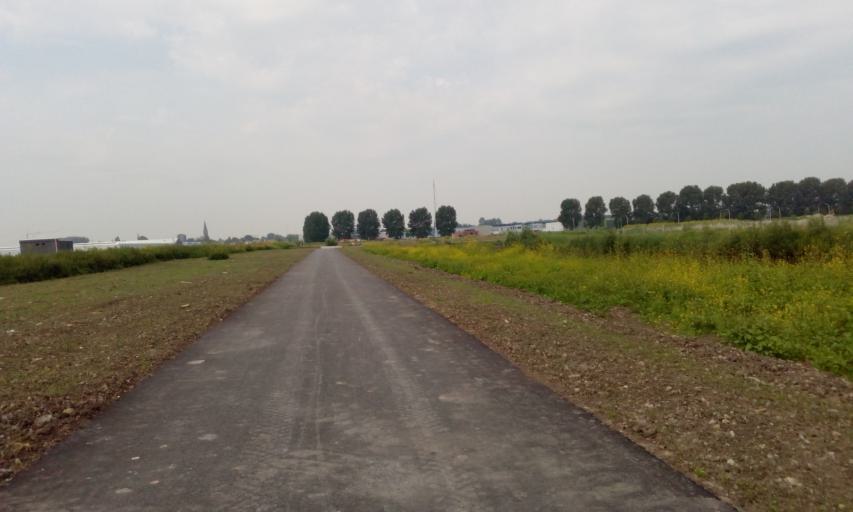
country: NL
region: South Holland
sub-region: Gemeente Pijnacker-Nootdorp
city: Pijnacker
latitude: 52.0279
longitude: 4.4513
